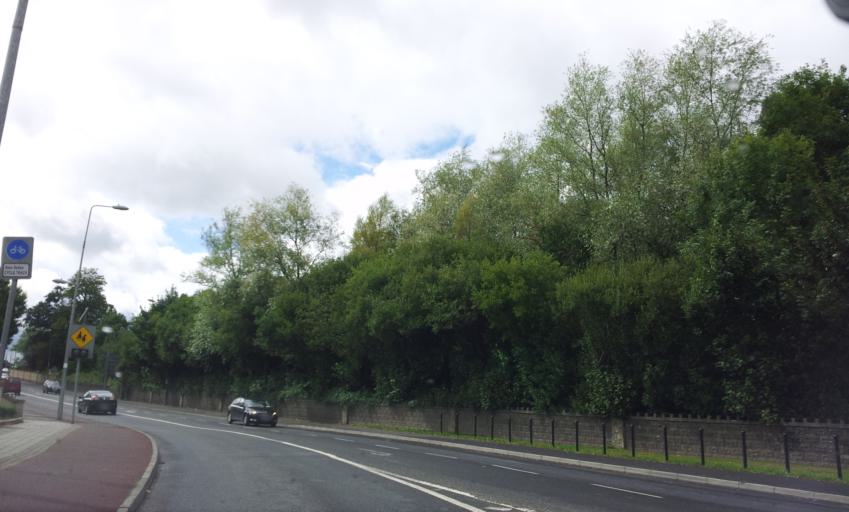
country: IE
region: Munster
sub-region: Waterford
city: Waterford
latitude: 52.2690
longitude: -7.0961
